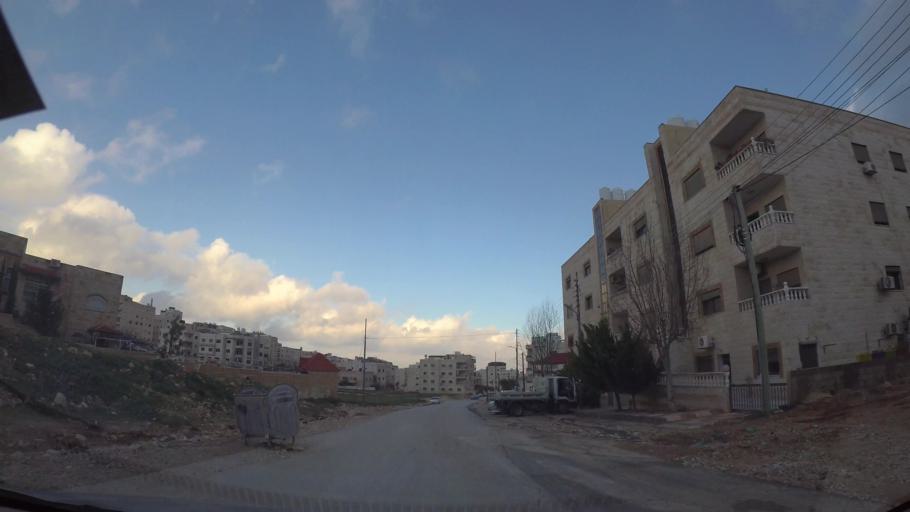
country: JO
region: Amman
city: Al Jubayhah
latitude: 32.0513
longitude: 35.8915
